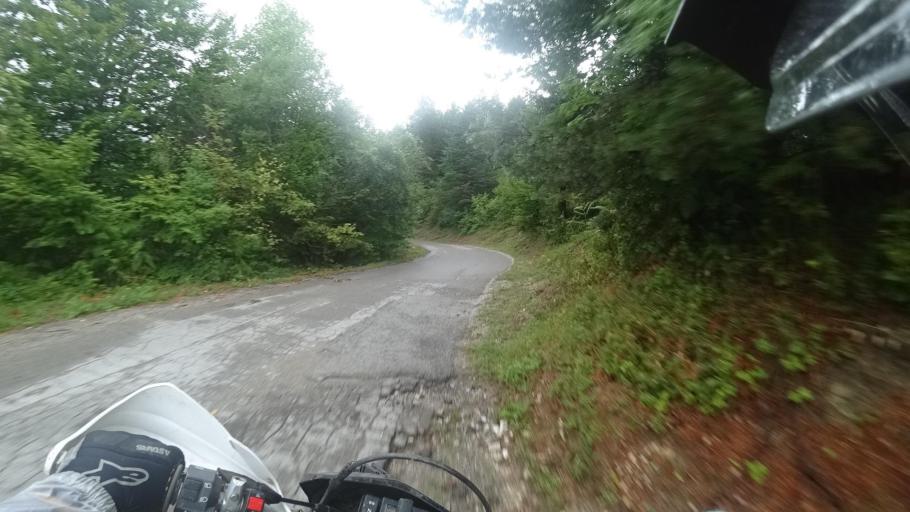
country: HR
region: Karlovacka
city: Plaski
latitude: 44.9974
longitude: 15.4129
